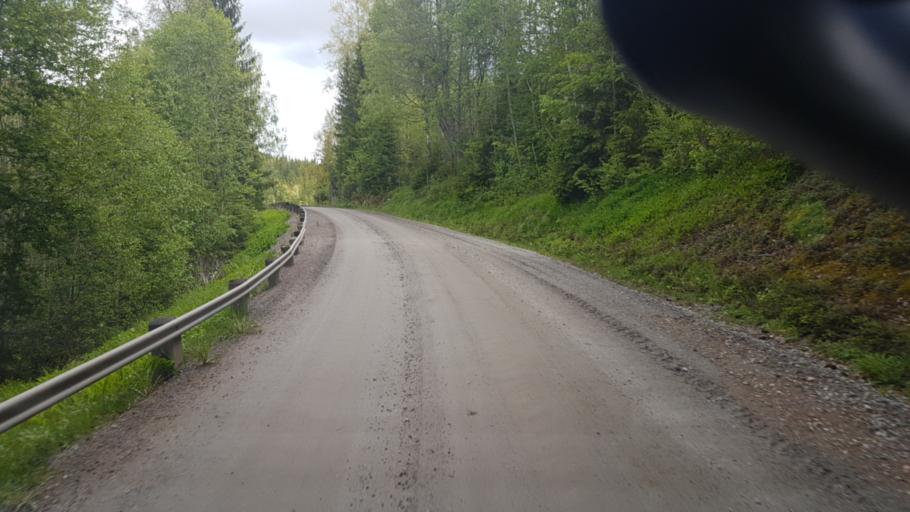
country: NO
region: Ostfold
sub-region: Romskog
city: Romskog
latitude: 59.7067
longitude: 11.9621
